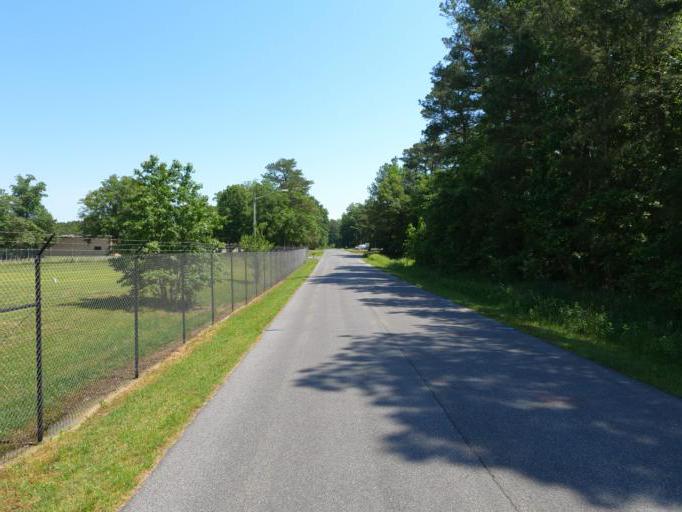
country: US
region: Delaware
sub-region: Sussex County
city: Georgetown
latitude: 38.6925
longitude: -75.3531
